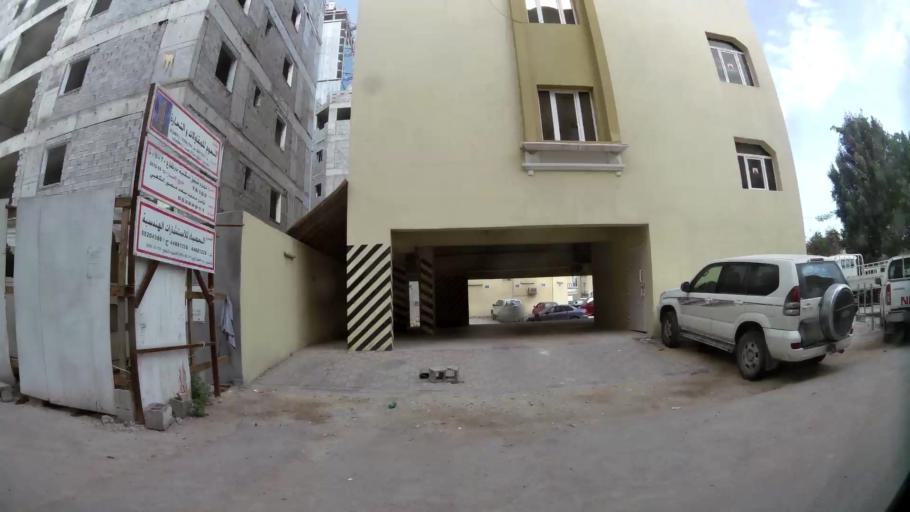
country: QA
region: Baladiyat ad Dawhah
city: Doha
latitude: 25.2850
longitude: 51.5156
